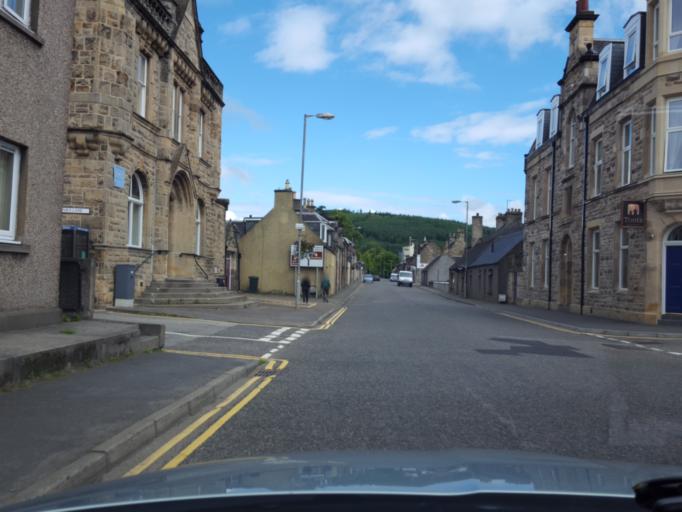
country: GB
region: Scotland
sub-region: Moray
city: Rothes
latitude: 57.5285
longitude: -3.2083
